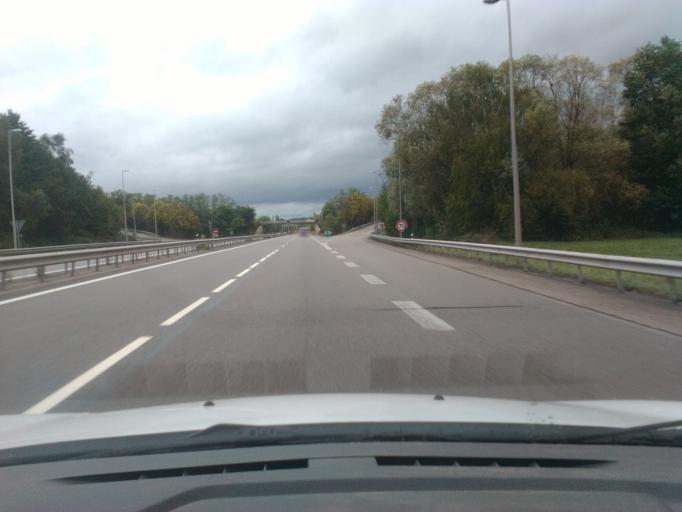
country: FR
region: Lorraine
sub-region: Departement des Vosges
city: Saint-Michel-sur-Meurthe
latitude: 48.3074
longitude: 6.9225
